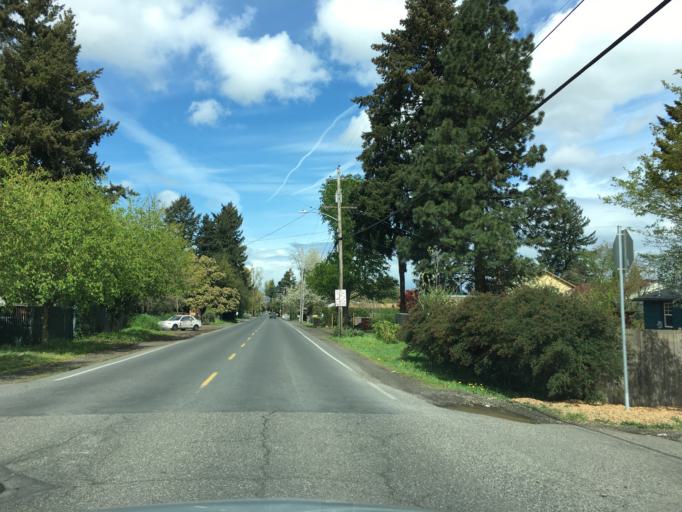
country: US
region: Oregon
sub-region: Multnomah County
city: Portland
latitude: 45.5567
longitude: -122.6009
